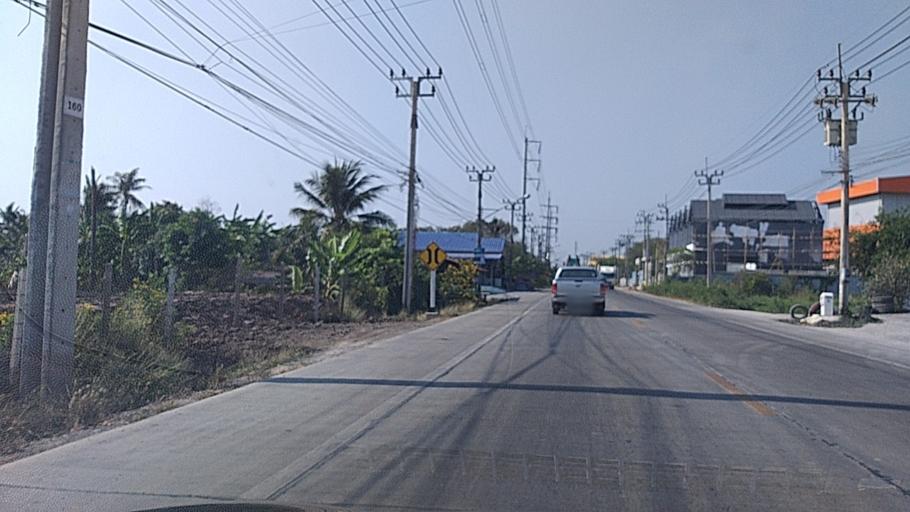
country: TH
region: Nonthaburi
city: Sai Noi
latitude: 13.9065
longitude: 100.3239
